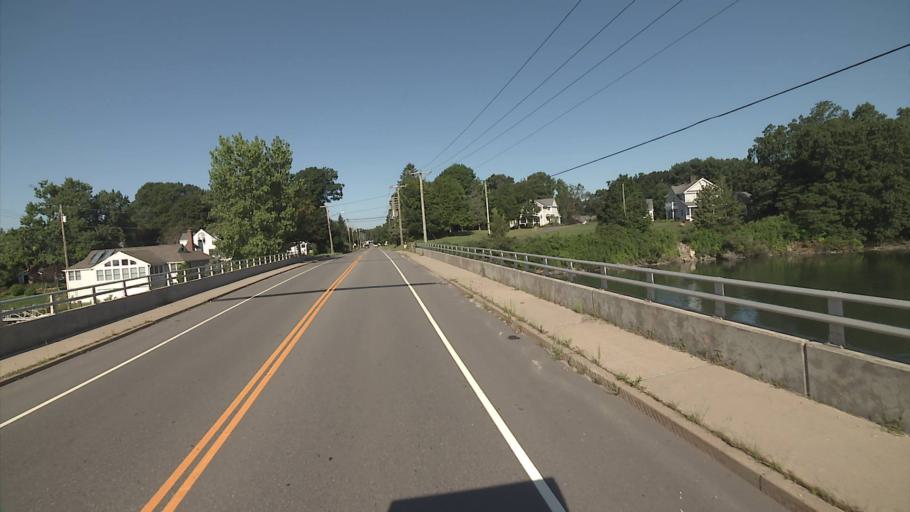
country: US
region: Connecticut
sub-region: Middlesex County
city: Westbrook Center
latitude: 41.2749
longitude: -72.4766
